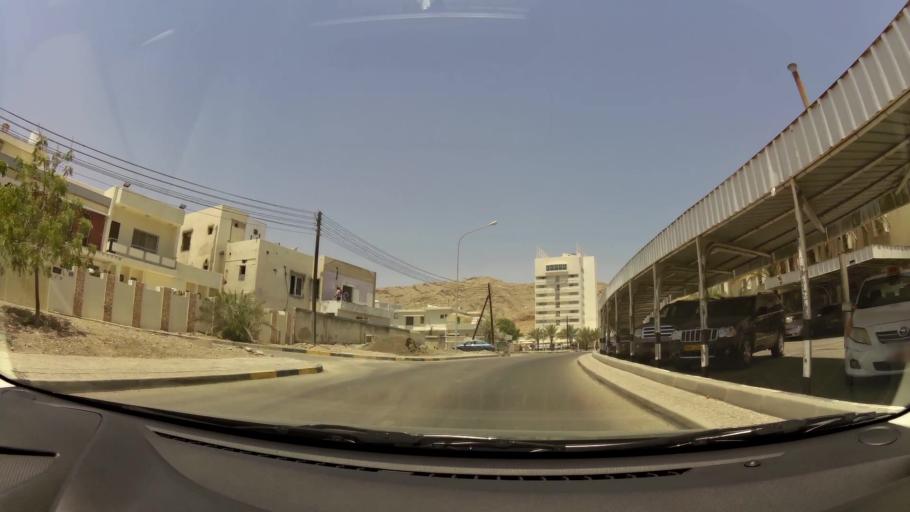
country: OM
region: Muhafazat Masqat
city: Muscat
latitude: 23.6065
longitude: 58.5404
